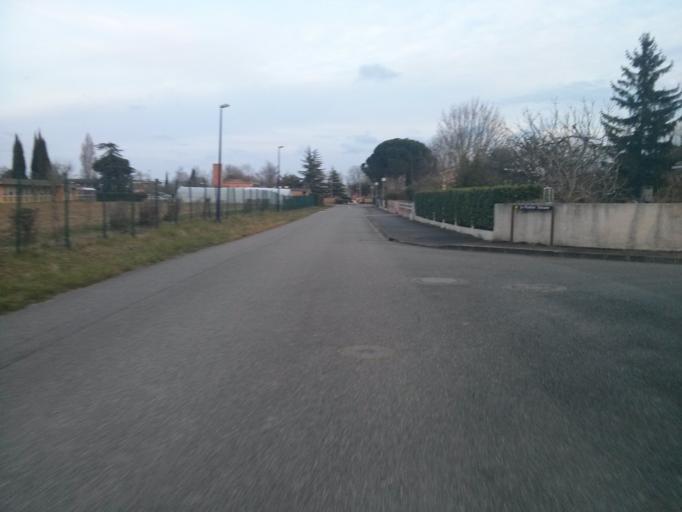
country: FR
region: Midi-Pyrenees
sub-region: Departement de la Haute-Garonne
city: Castanet-Tolosan
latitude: 43.5291
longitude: 1.4978
